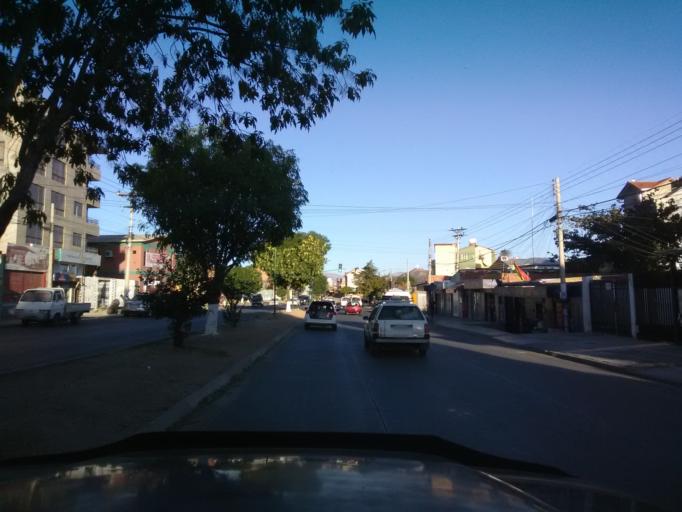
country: BO
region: Cochabamba
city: Cochabamba
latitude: -17.3589
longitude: -66.1728
